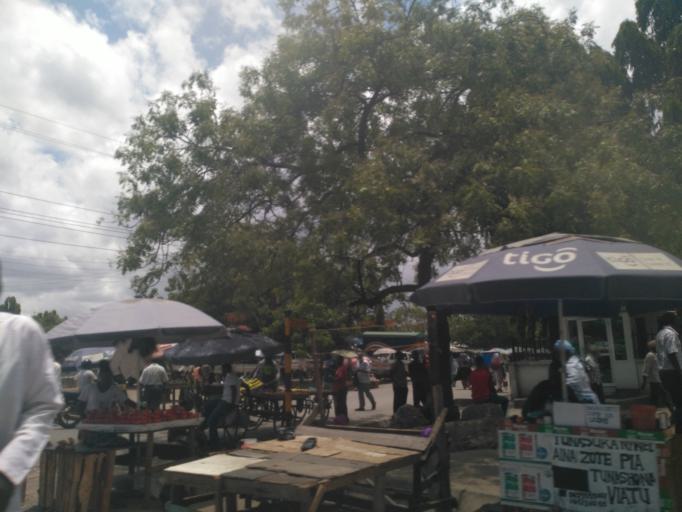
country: TZ
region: Dar es Salaam
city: Dar es Salaam
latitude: -6.8608
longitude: 39.2633
